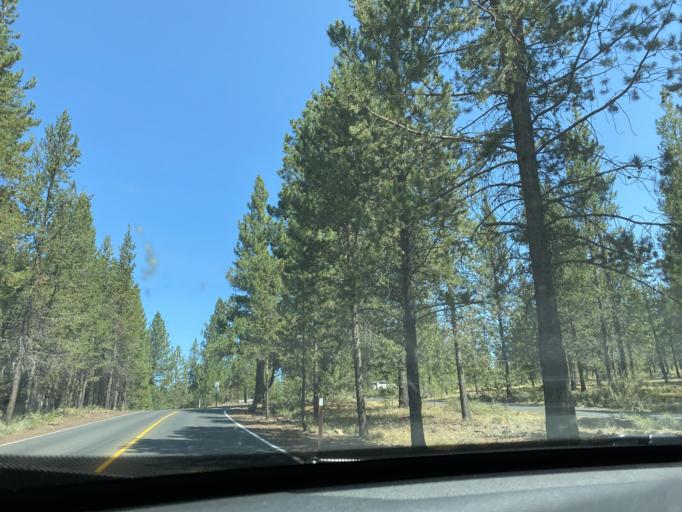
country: US
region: Oregon
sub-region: Deschutes County
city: Sunriver
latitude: 43.8888
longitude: -121.4384
